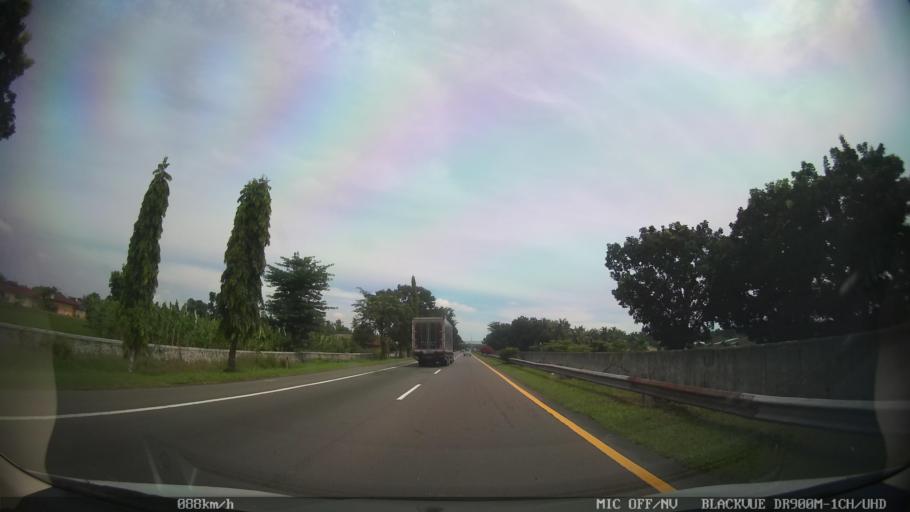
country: ID
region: North Sumatra
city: Labuhan Deli
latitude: 3.6939
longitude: 98.6820
